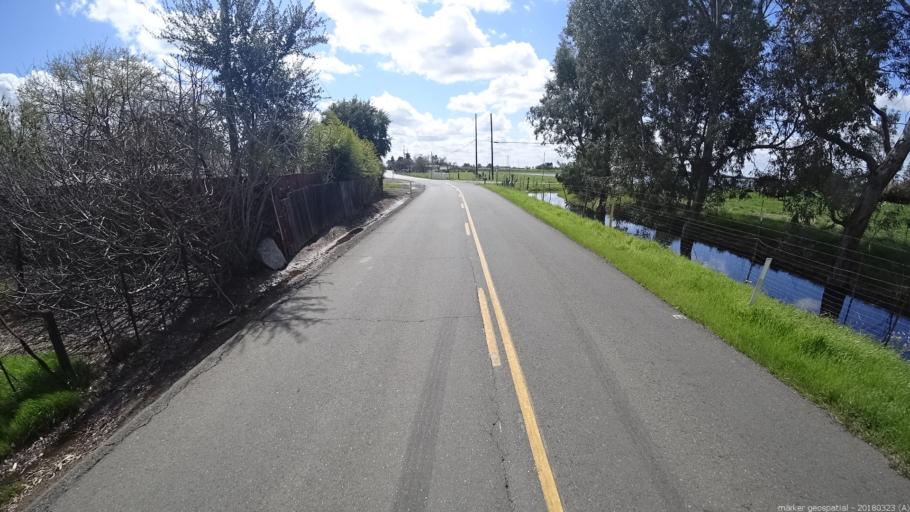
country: US
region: California
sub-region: Sacramento County
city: Elverta
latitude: 38.7004
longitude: -121.4754
